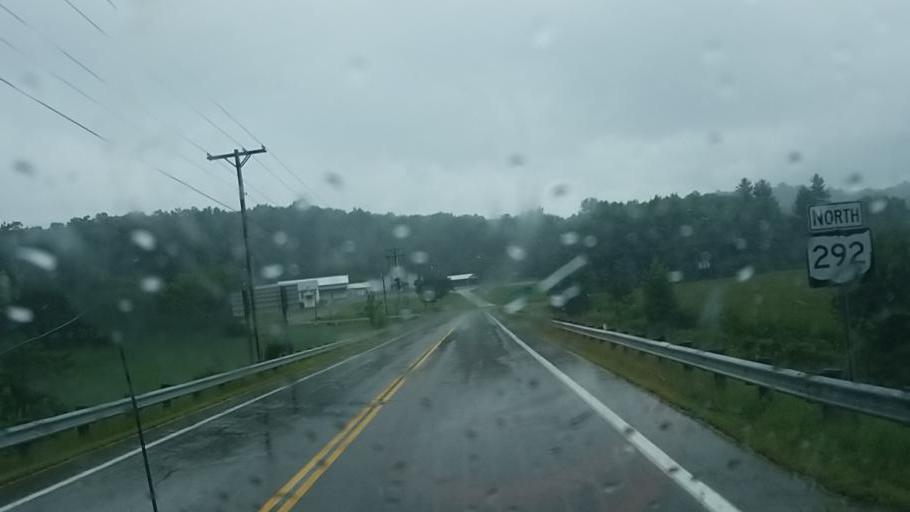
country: US
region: Ohio
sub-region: Logan County
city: Bellefontaine
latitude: 40.3264
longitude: -83.6628
